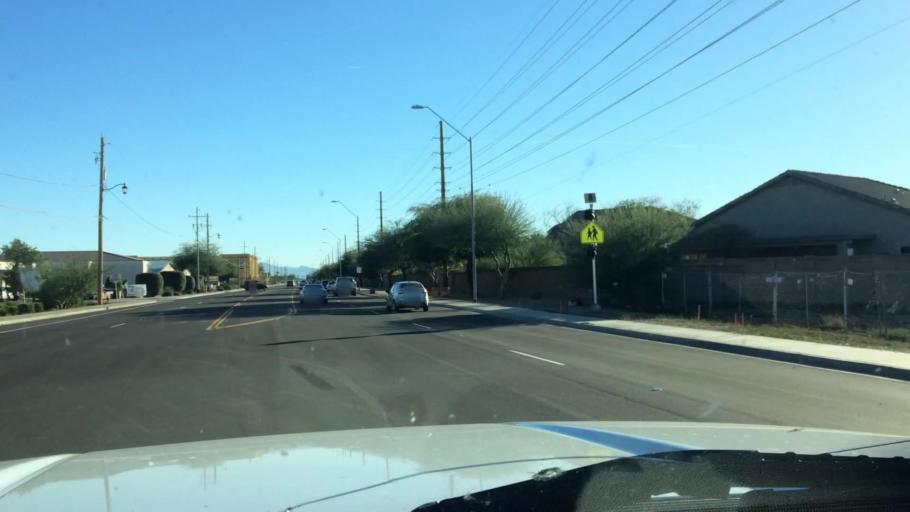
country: US
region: Arizona
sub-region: Maricopa County
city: Surprise
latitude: 33.6309
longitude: -112.3421
